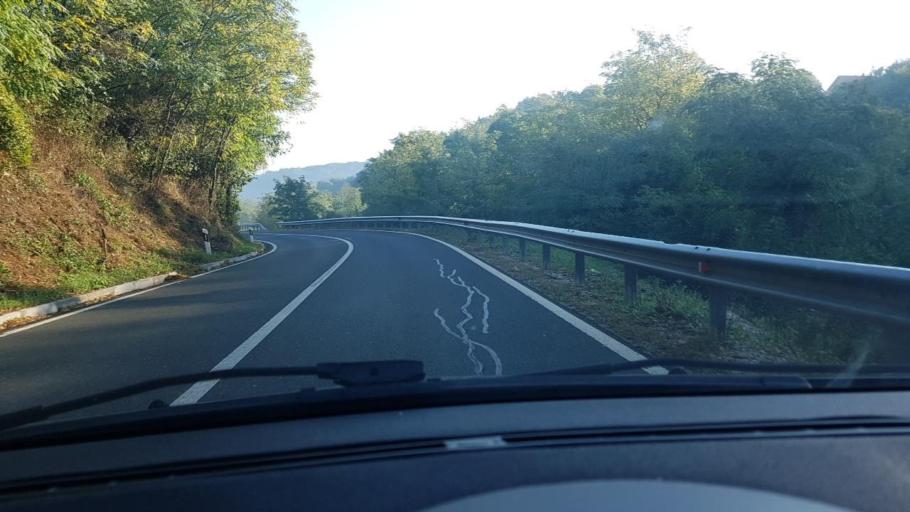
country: HR
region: Krapinsko-Zagorska
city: Marija Bistrica
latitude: 45.9762
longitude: 16.1043
